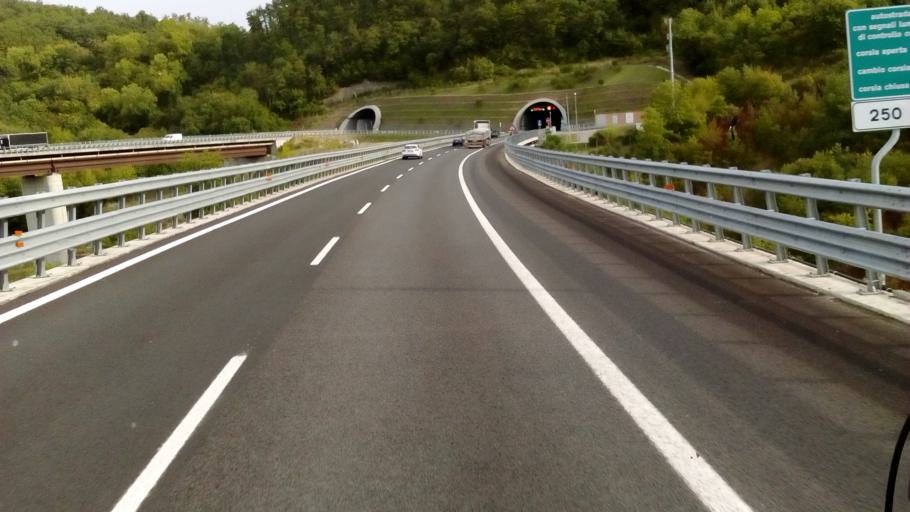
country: IT
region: Tuscany
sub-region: Province of Florence
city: Barberino di Mugello
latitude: 44.0365
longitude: 11.2268
